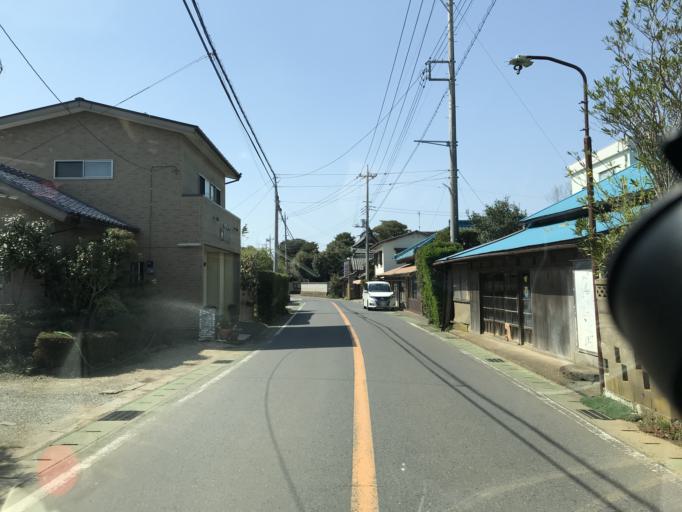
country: JP
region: Chiba
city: Asahi
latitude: 35.7919
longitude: 140.6787
